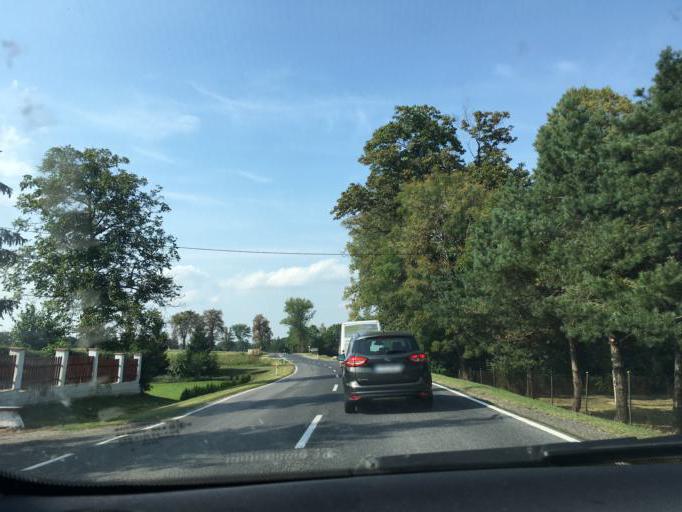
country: PL
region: Opole Voivodeship
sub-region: Powiat prudnicki
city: Laka Prudnicka
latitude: 50.3744
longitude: 17.5352
